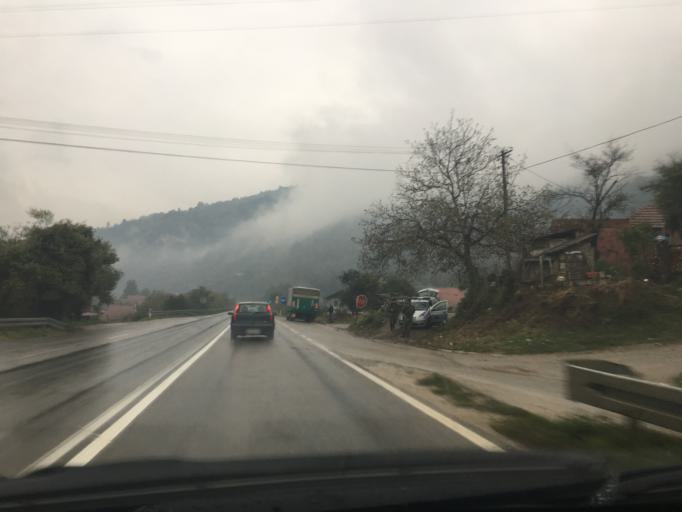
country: RS
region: Central Serbia
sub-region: Pcinjski Okrug
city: Vladicin Han
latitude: 42.7743
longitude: 22.0918
